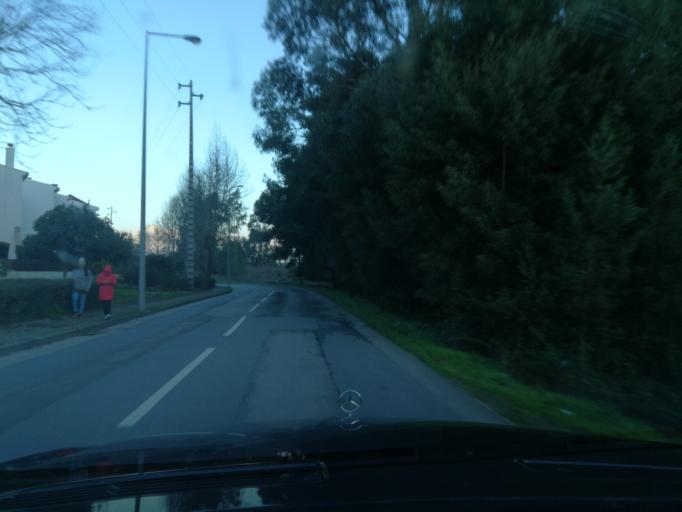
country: PT
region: Aveiro
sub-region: Estarreja
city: Estarreja
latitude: 40.7575
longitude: -8.5919
